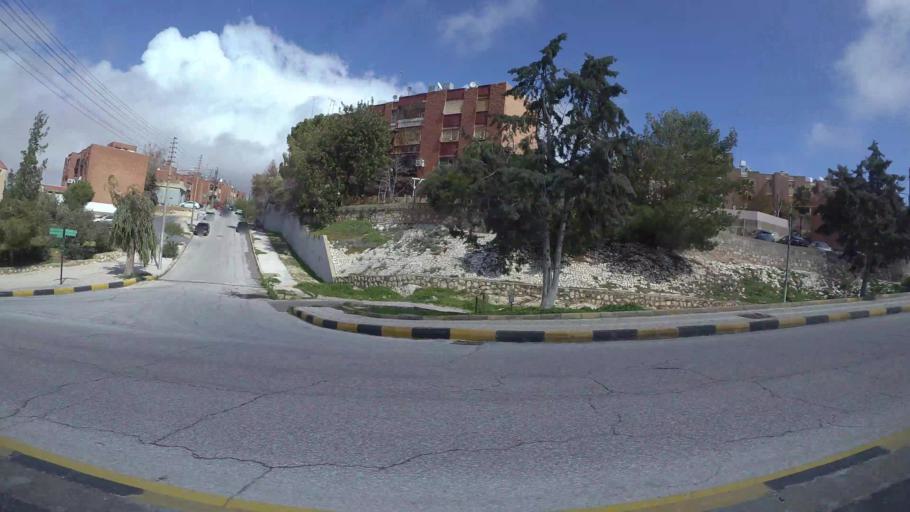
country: JO
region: Amman
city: Al Jubayhah
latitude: 32.0545
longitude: 35.8743
